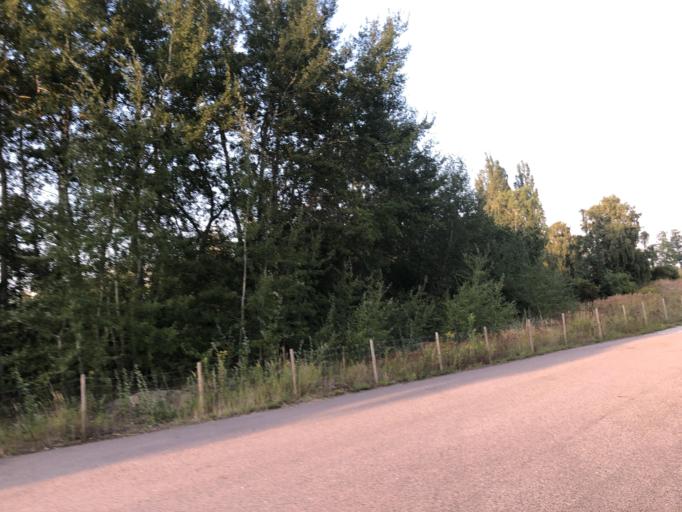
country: SE
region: Skane
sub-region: Malmo
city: Malmoe
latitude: 55.6033
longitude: 13.0409
